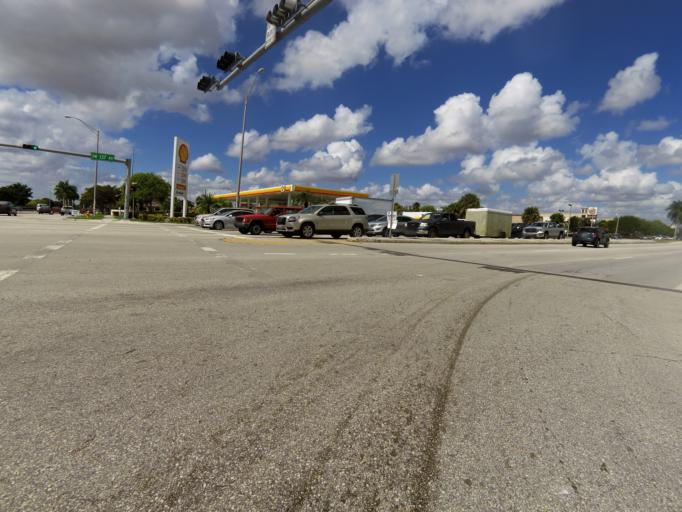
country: US
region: Florida
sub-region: Miami-Dade County
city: Kendale Lakes
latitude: 25.7292
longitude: -80.4155
